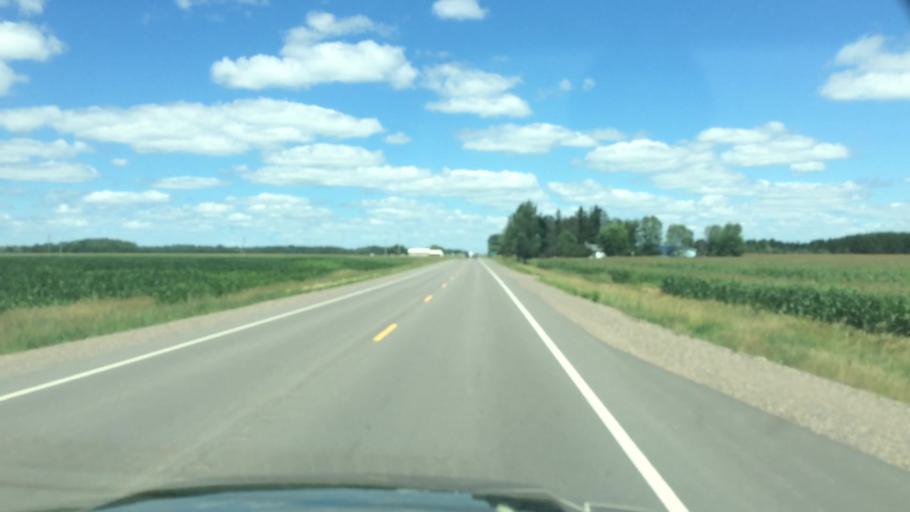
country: US
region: Wisconsin
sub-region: Clark County
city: Abbotsford
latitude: 45.0295
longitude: -90.3150
